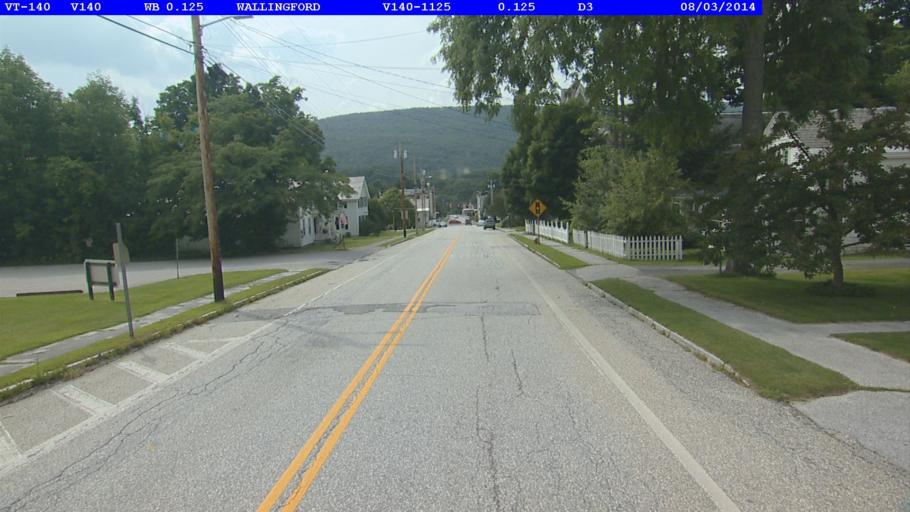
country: US
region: Vermont
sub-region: Rutland County
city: Rutland
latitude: 43.4713
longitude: -72.9748
